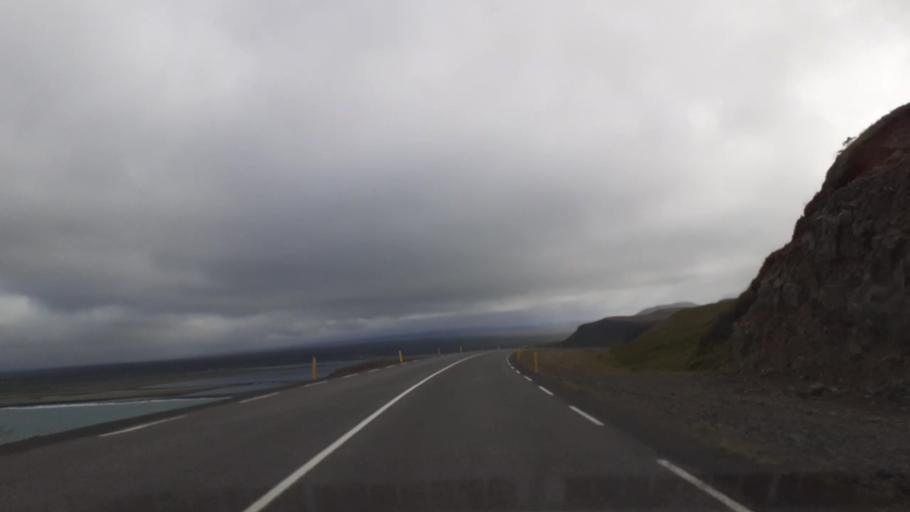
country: IS
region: Northeast
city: Husavik
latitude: 66.1358
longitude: -16.9509
